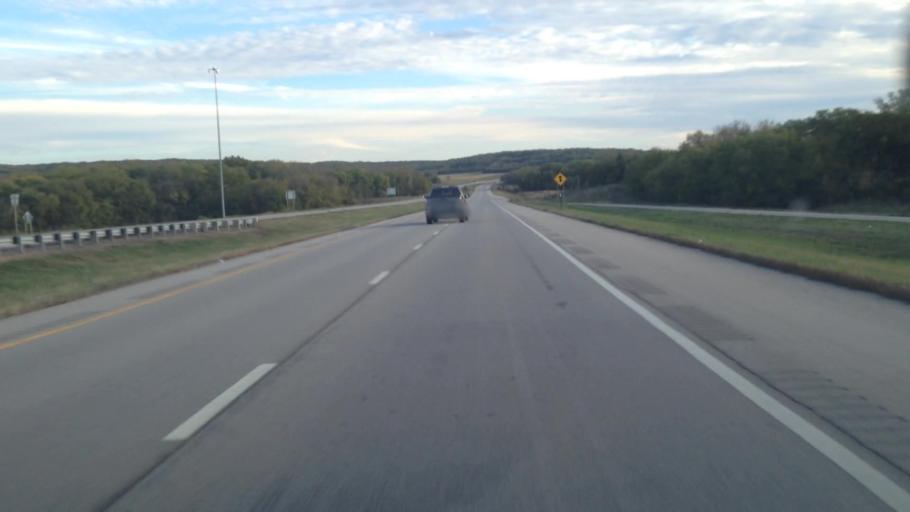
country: US
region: Kansas
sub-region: Douglas County
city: Lawrence
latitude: 38.8840
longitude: -95.2584
